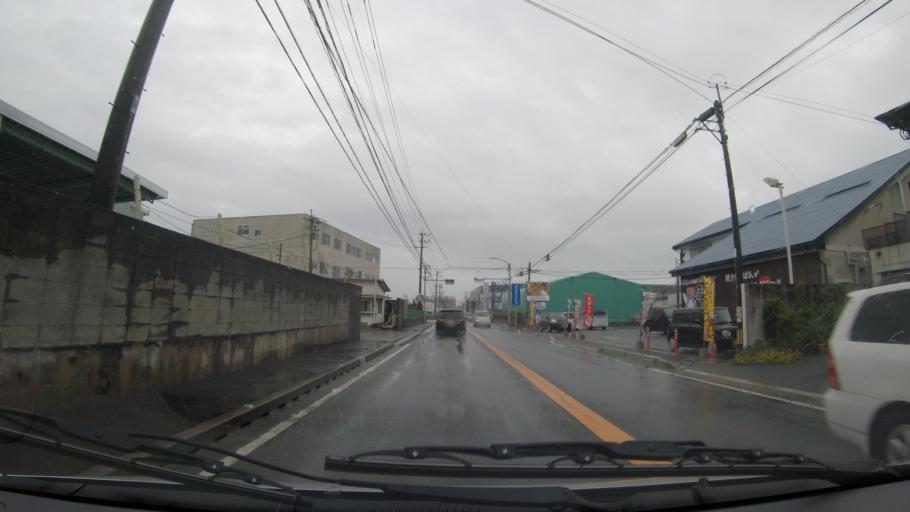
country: JP
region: Fukuoka
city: Koga
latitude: 33.7206
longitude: 130.4547
